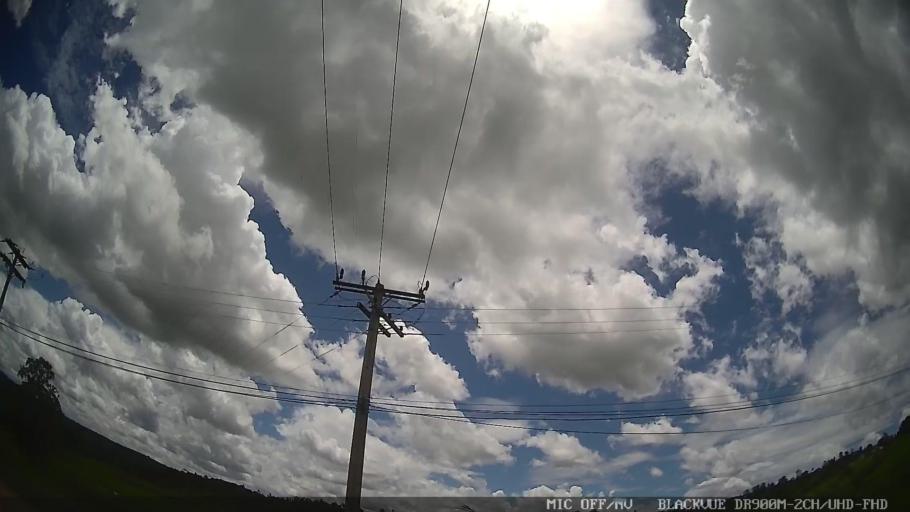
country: BR
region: Sao Paulo
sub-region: Pedreira
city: Pedreira
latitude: -22.7269
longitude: -46.9342
